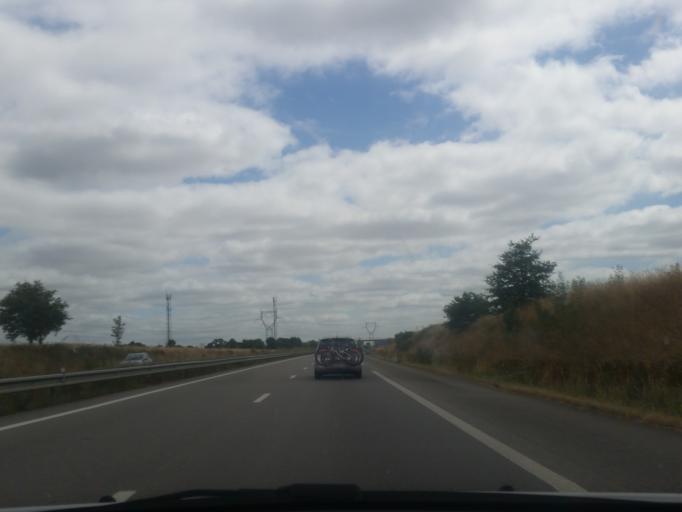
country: FR
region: Pays de la Loire
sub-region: Departement de la Loire-Atlantique
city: Varades
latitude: 47.4219
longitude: -1.0525
